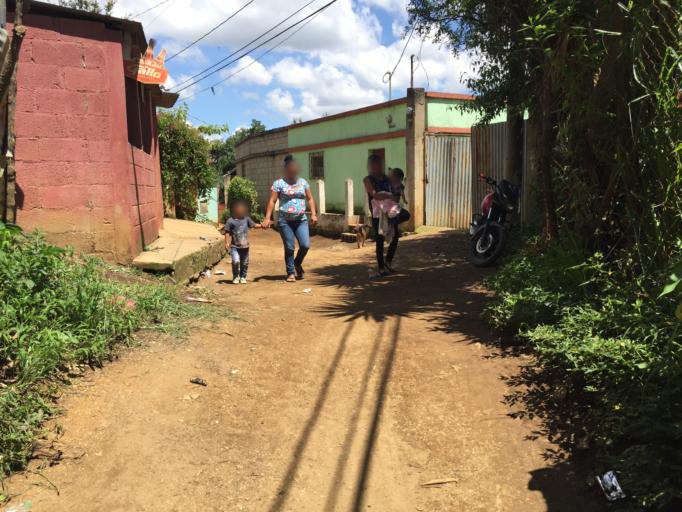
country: GT
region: Guatemala
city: Amatitlan
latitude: 14.5086
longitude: -90.6496
